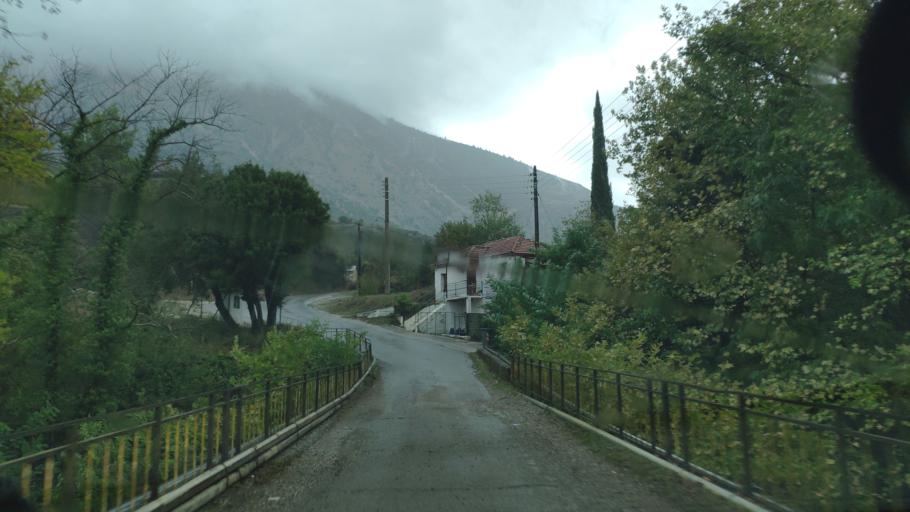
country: GR
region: West Greece
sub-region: Nomos Aitolias kai Akarnanias
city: Krikellos
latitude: 39.0264
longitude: 21.3132
